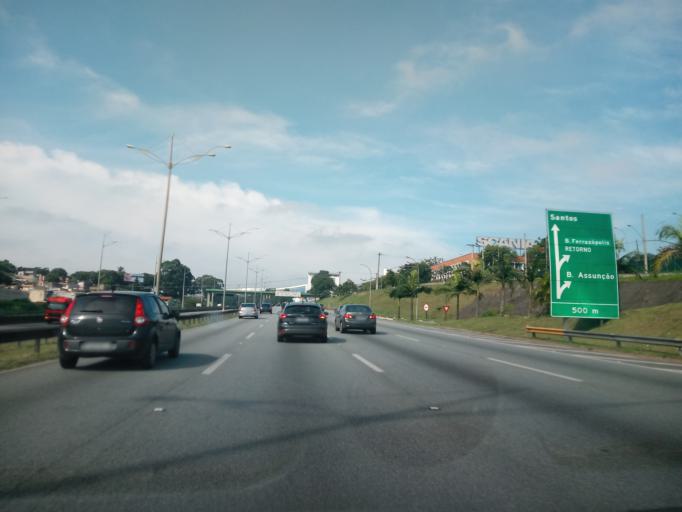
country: BR
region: Sao Paulo
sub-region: Sao Bernardo Do Campo
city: Sao Bernardo do Campo
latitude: -23.7102
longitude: -46.5616
